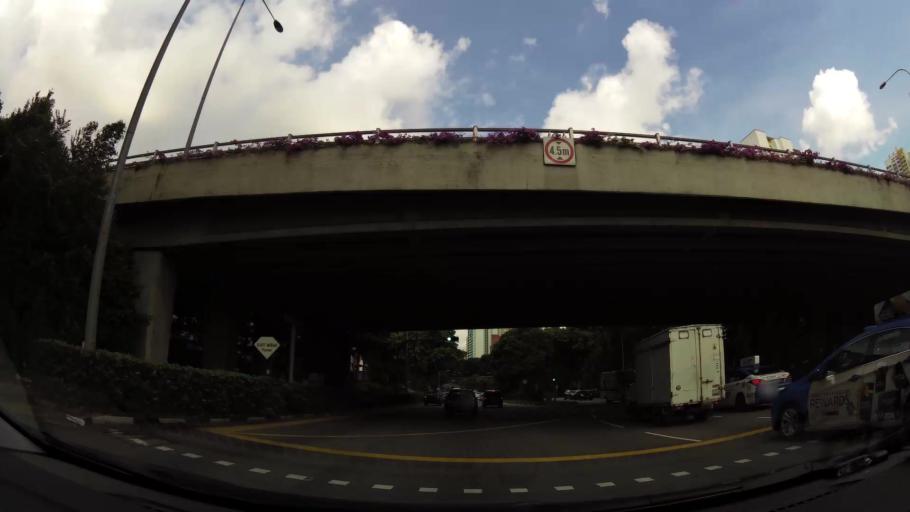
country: SG
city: Singapore
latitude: 1.2789
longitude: 103.8291
